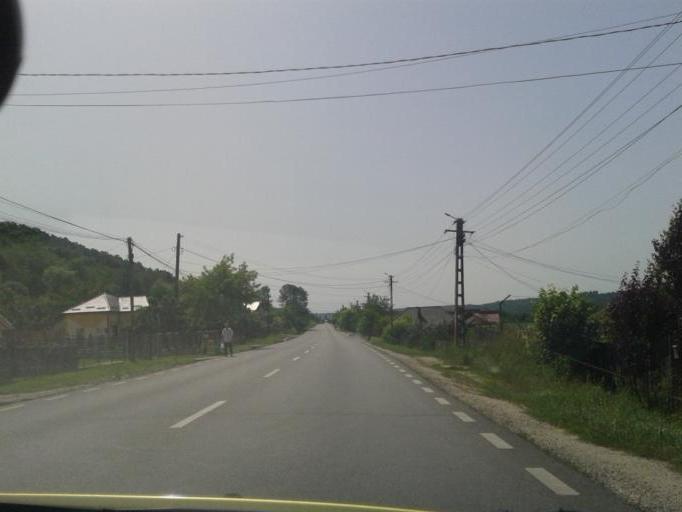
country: RO
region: Arges
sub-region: Comuna Babana
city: Babana
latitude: 44.9069
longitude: 24.7278
